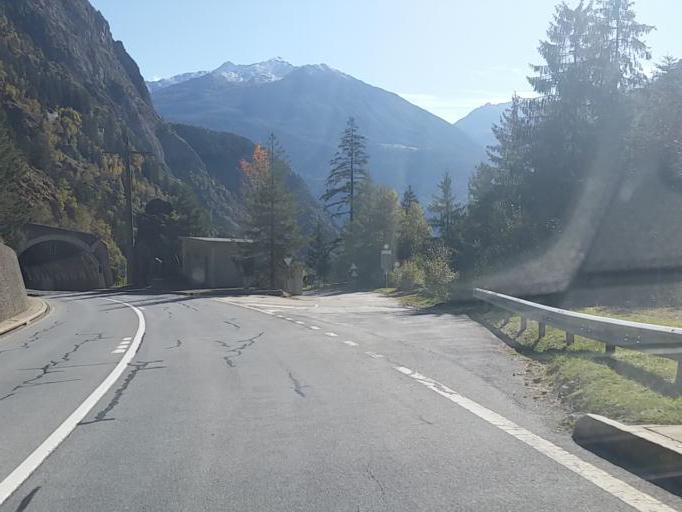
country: CH
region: Valais
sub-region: Leuk District
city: Gampel
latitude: 46.3431
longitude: 7.7543
